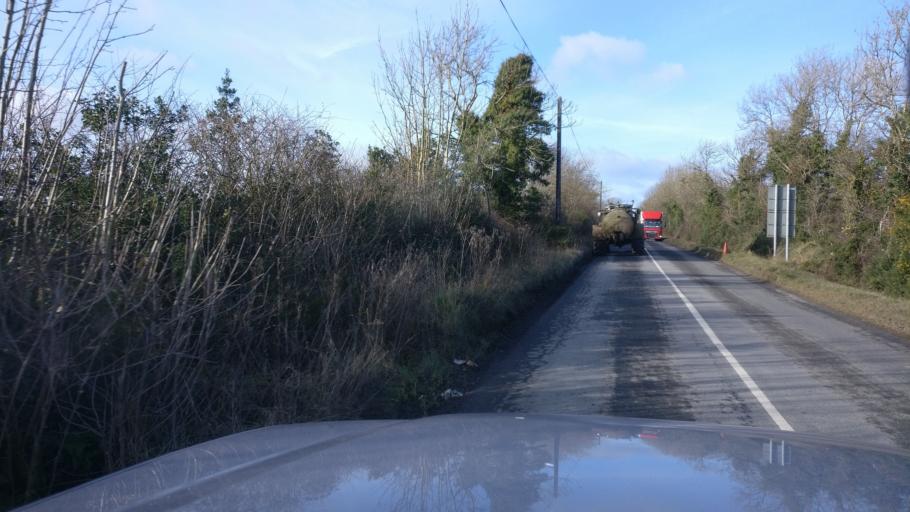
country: IE
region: Leinster
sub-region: Kilkenny
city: Castlecomer
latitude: 52.8933
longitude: -7.1684
